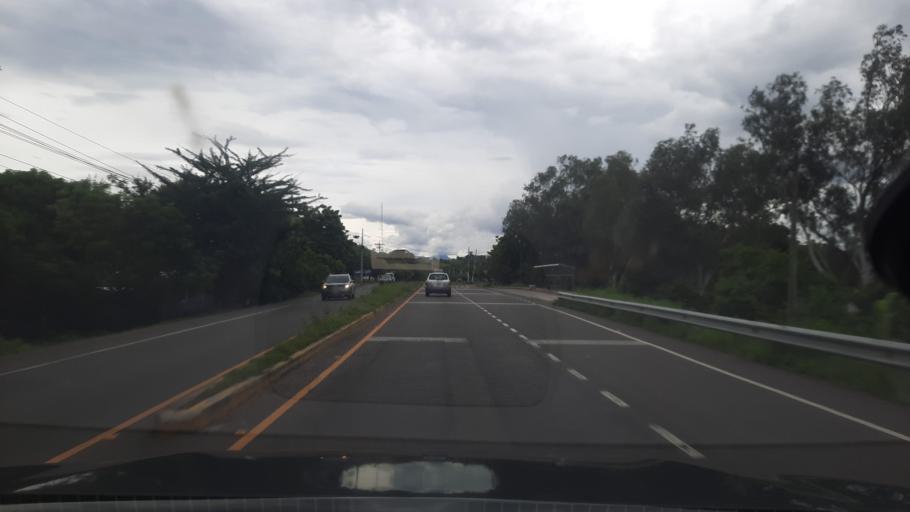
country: HN
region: Choluteca
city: Ciudad Choluteca
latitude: 13.3436
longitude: -87.2553
